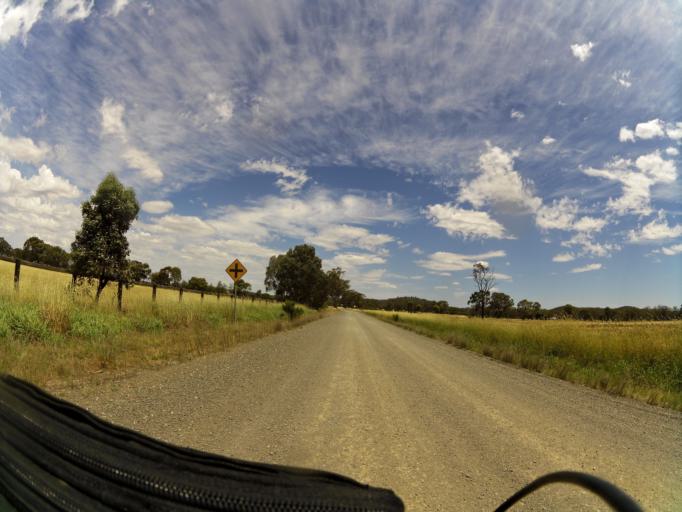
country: AU
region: Victoria
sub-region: Campaspe
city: Kyabram
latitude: -36.7573
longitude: 145.1026
